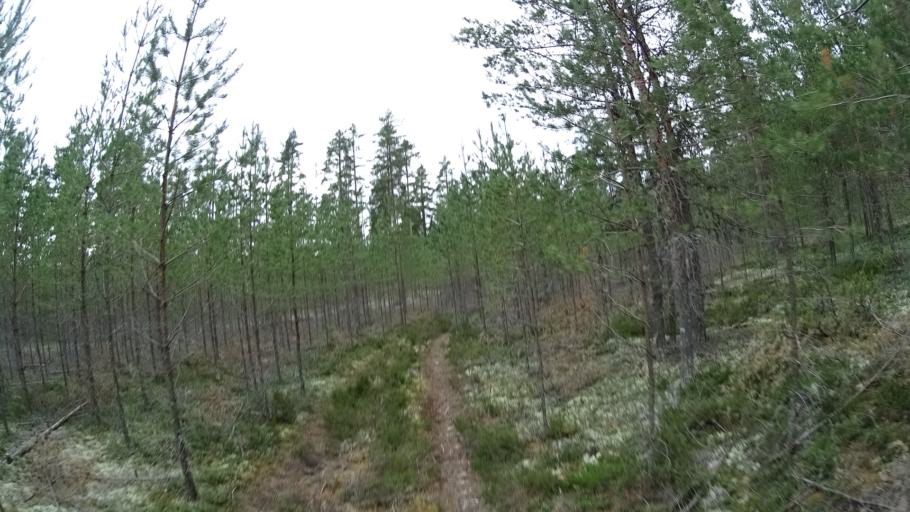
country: FI
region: Satakunta
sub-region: Pohjois-Satakunta
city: Jaemijaervi
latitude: 61.7647
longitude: 22.7607
